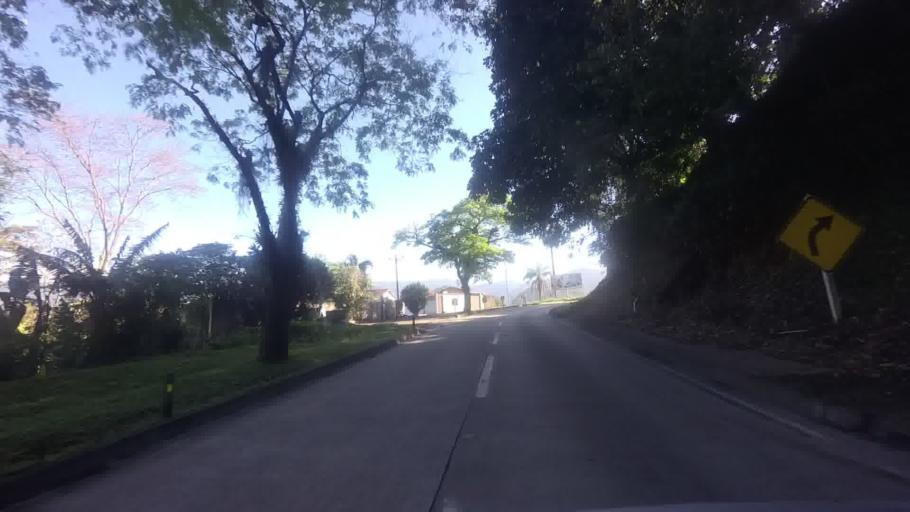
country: BR
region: Rio de Janeiro
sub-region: Petropolis
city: Petropolis
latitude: -22.5739
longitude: -43.2597
